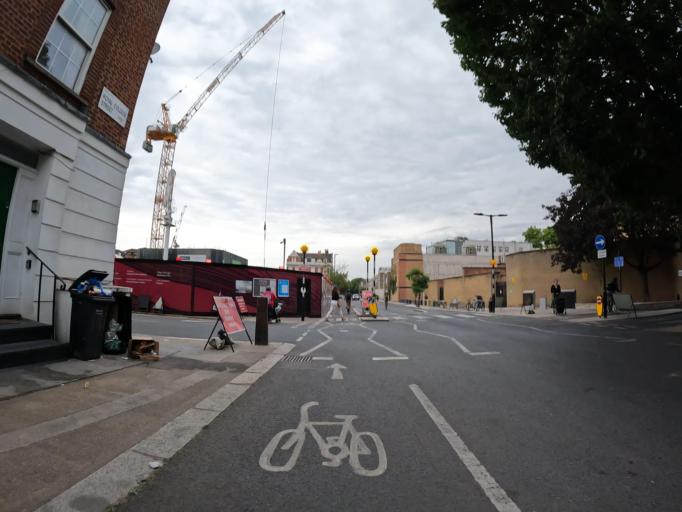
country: GB
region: England
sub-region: Greater London
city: Camden Town
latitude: 51.5403
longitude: -0.1370
